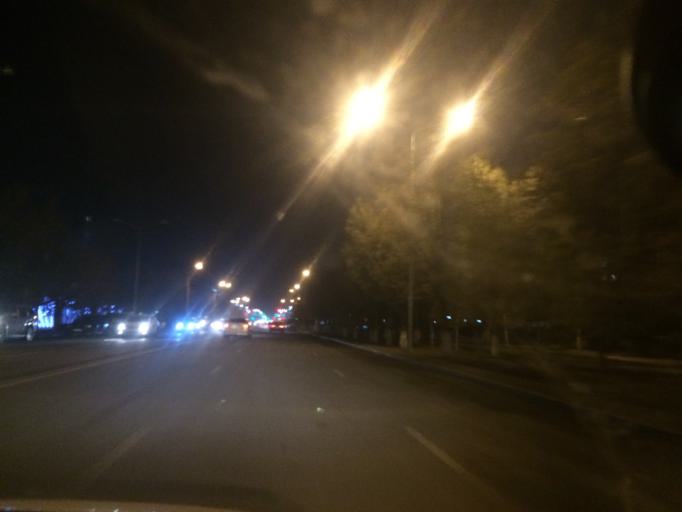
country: KZ
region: Astana Qalasy
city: Astana
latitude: 51.1739
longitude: 71.4193
